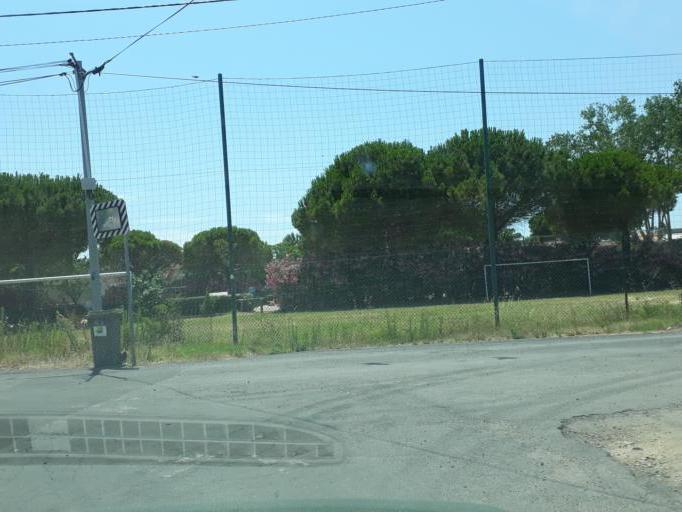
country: FR
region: Languedoc-Roussillon
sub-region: Departement de l'Herault
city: Agde
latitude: 43.2877
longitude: 3.4511
